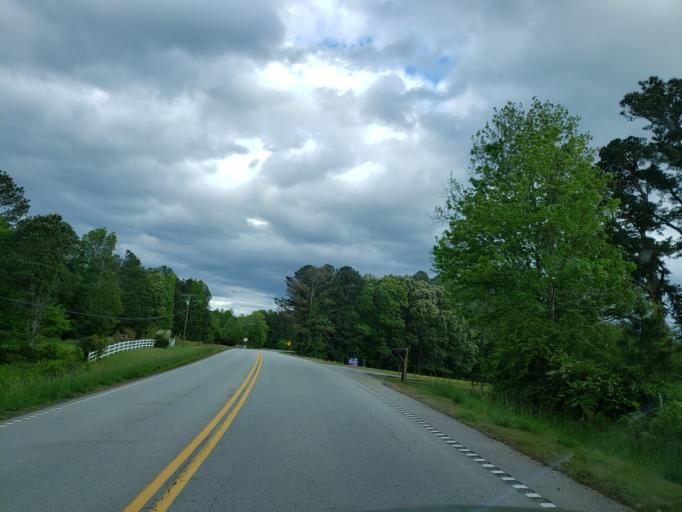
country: US
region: Georgia
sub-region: Haralson County
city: Tallapoosa
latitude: 33.8657
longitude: -85.2990
